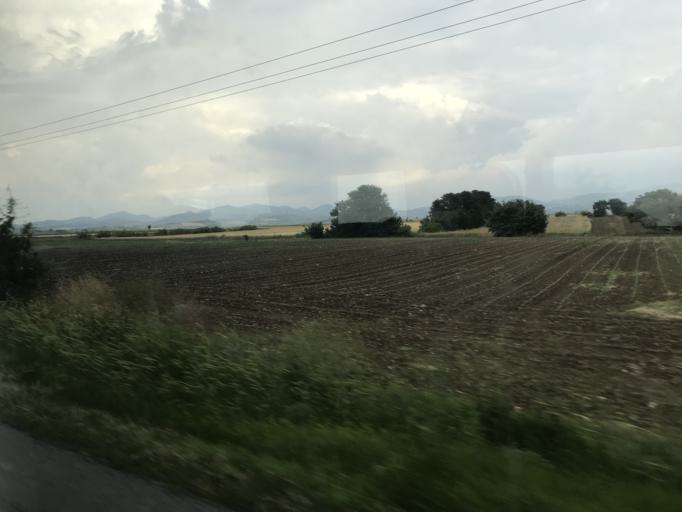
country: GR
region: East Macedonia and Thrace
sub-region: Nomos Rodopis
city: Sapes
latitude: 40.9858
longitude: 25.6534
